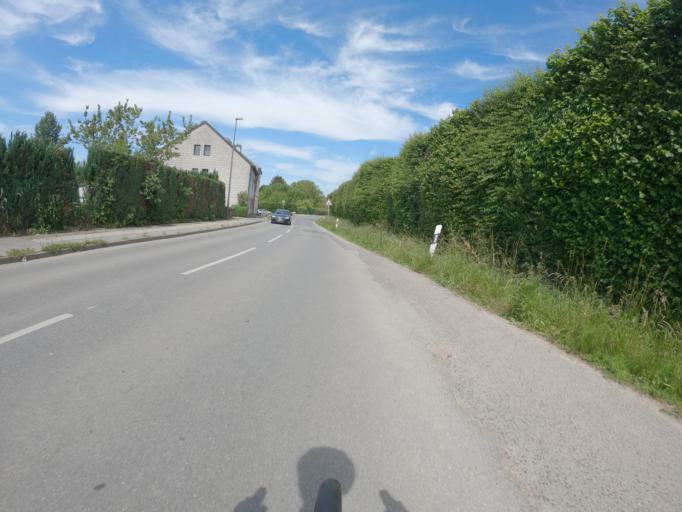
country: BE
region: Wallonia
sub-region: Province de Liege
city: Raeren
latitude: 50.7313
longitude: 6.1416
